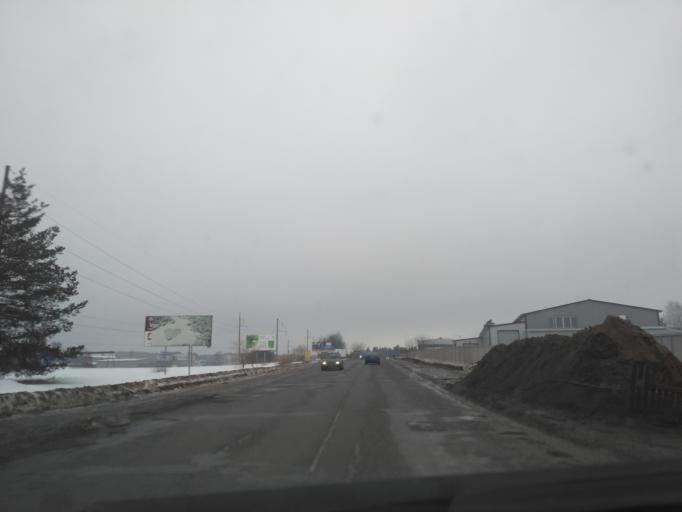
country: BY
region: Minsk
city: Horad Barysaw
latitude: 54.1990
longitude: 28.4937
